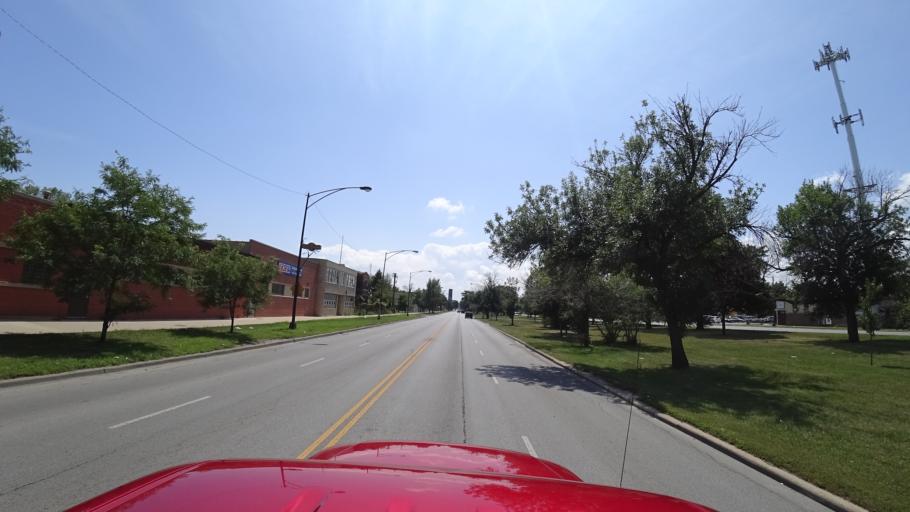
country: US
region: Illinois
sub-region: Cook County
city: Chicago
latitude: 41.8204
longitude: -87.6842
